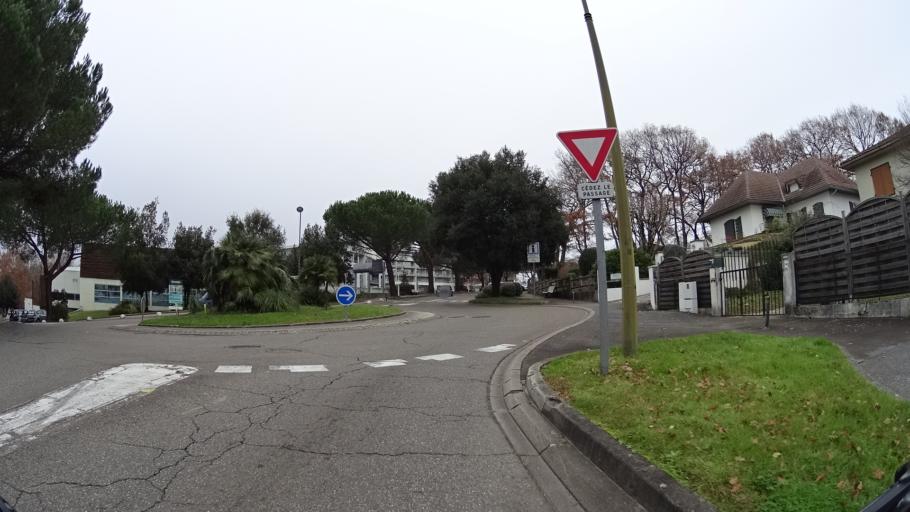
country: FR
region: Aquitaine
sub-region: Departement des Landes
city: Saint-Paul-les-Dax
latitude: 43.7273
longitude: -1.0631
